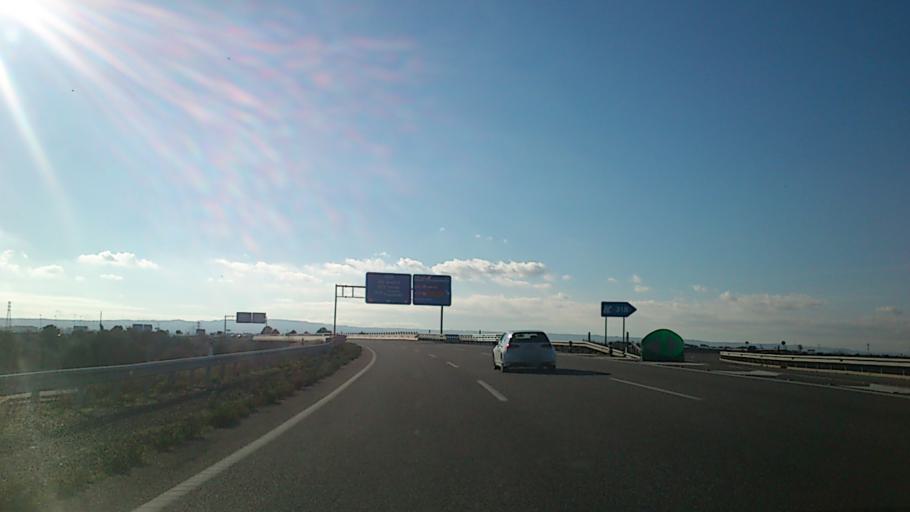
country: ES
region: Aragon
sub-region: Provincia de Zaragoza
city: Almozara
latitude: 41.6797
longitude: -0.9242
